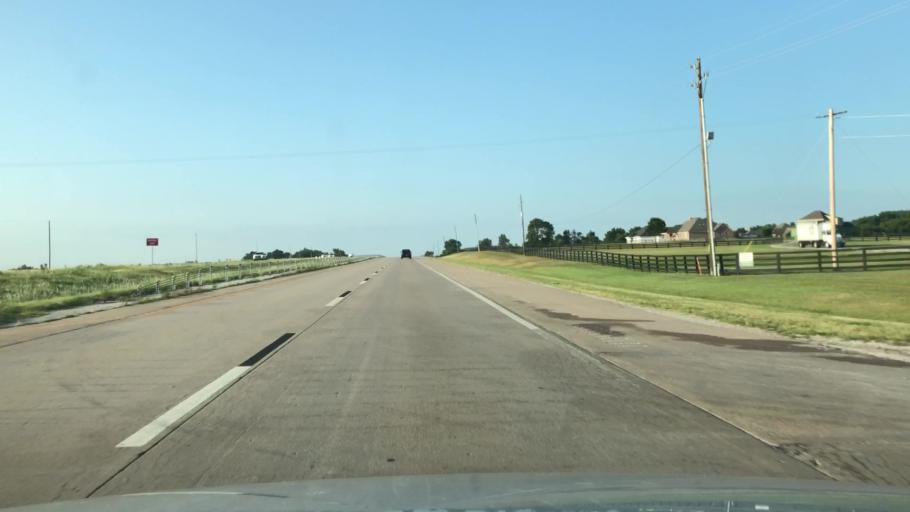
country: US
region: Oklahoma
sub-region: Osage County
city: Skiatook
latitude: 36.4671
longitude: -95.9207
